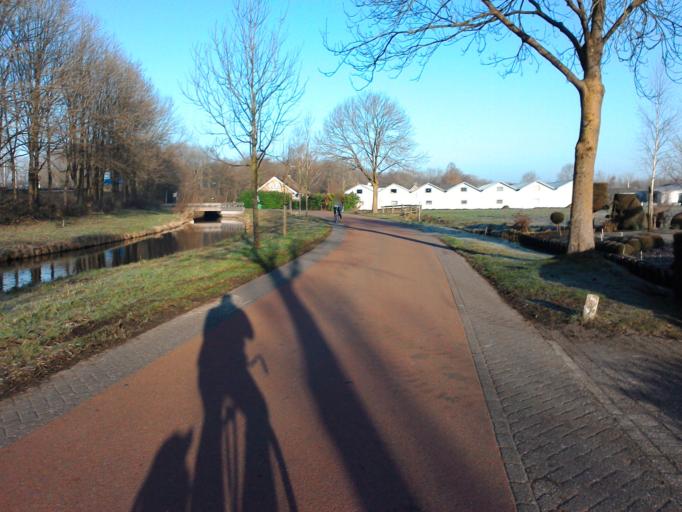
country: NL
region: Utrecht
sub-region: Stichtse Vecht
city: Maarssen
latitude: 52.1365
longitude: 5.0619
